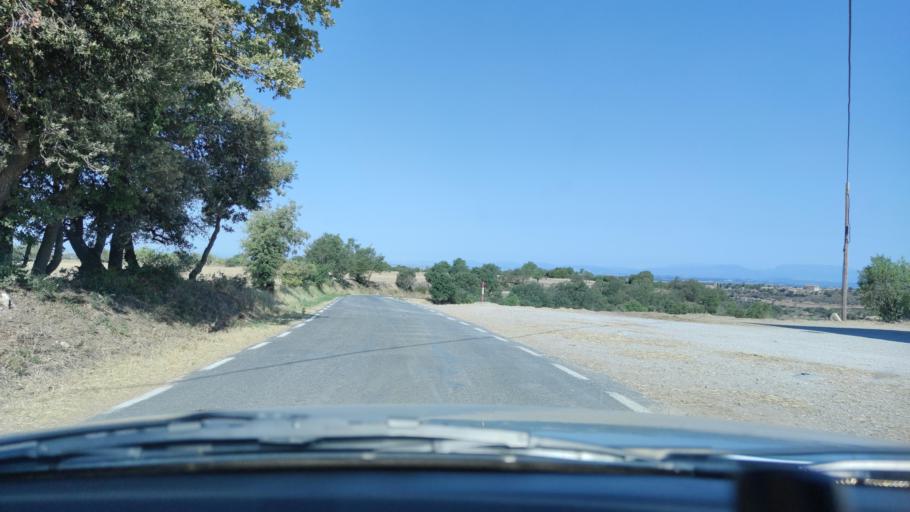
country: ES
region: Catalonia
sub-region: Provincia de Lleida
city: Ivorra
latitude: 41.7311
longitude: 1.3637
